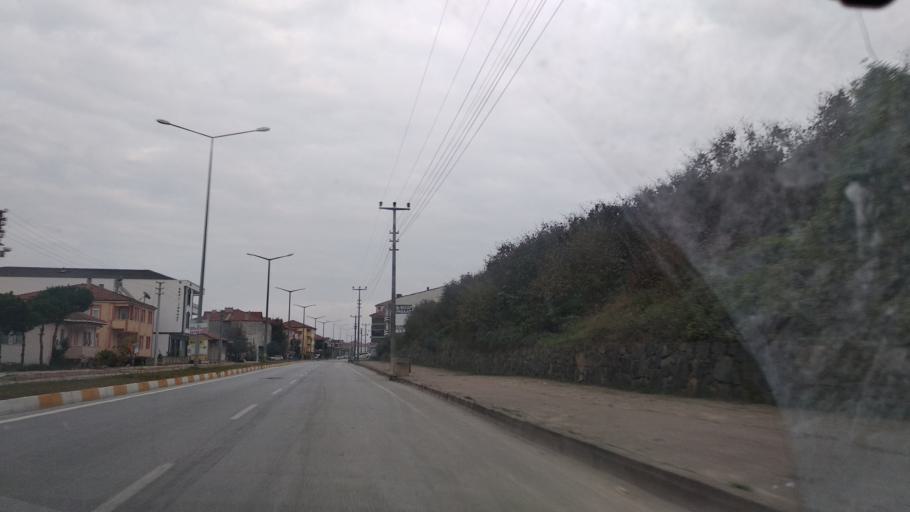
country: TR
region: Sakarya
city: Karasu
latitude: 41.0973
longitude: 30.6771
